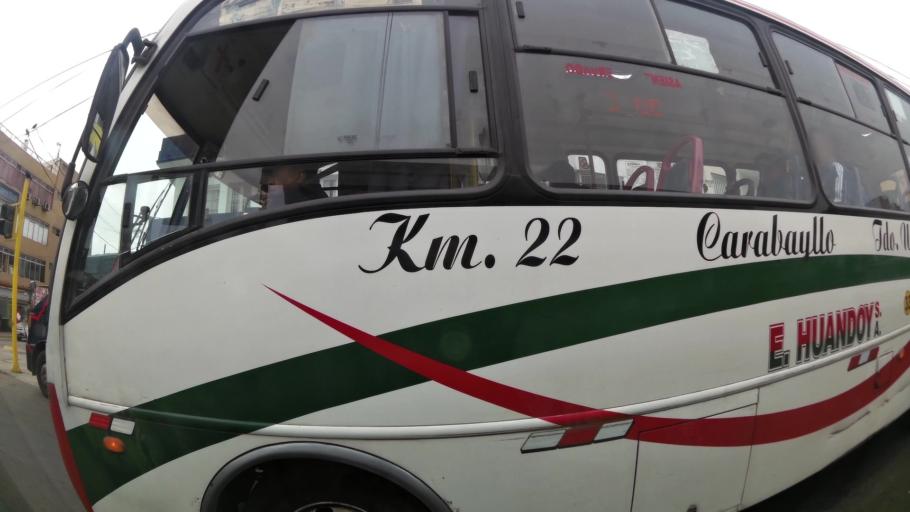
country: PE
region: Lima
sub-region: Lima
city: San Isidro
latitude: -12.0896
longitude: -77.0659
